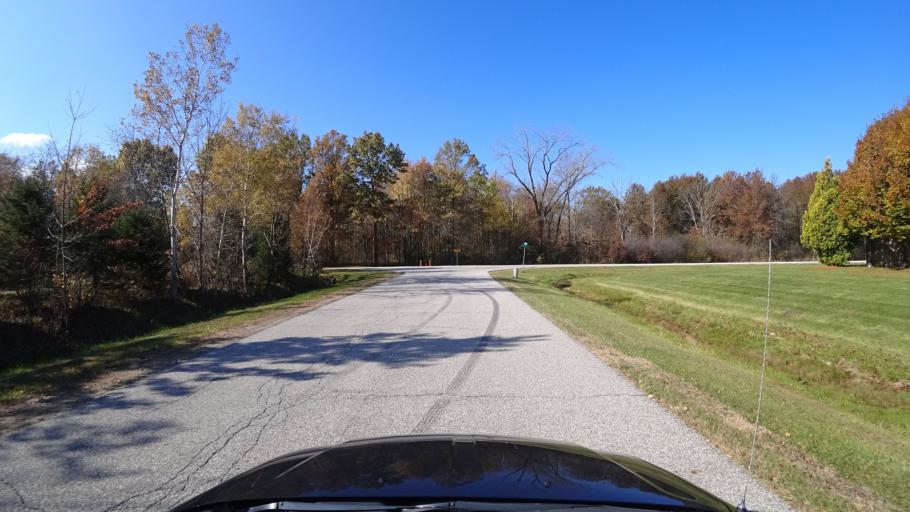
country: US
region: Indiana
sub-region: LaPorte County
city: Long Beach
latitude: 41.7329
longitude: -86.8303
